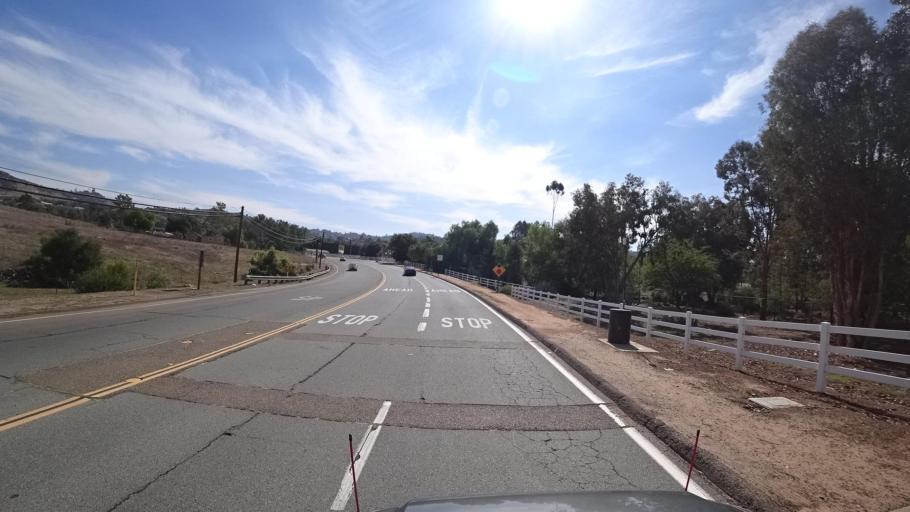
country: US
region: California
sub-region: San Diego County
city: Harbison Canyon
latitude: 32.8426
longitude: -116.8089
